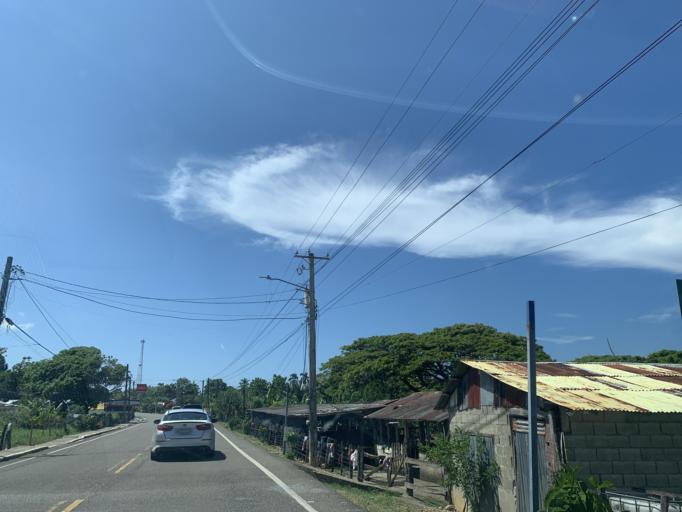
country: DO
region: Maria Trinidad Sanchez
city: Cabrera
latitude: 19.6700
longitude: -69.9537
